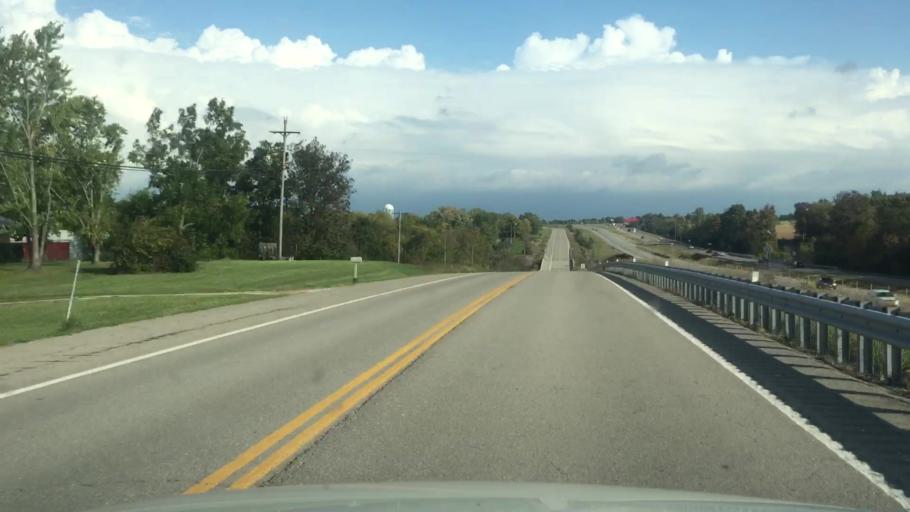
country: US
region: Missouri
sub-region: Boone County
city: Ashland
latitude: 38.8509
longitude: -92.2502
